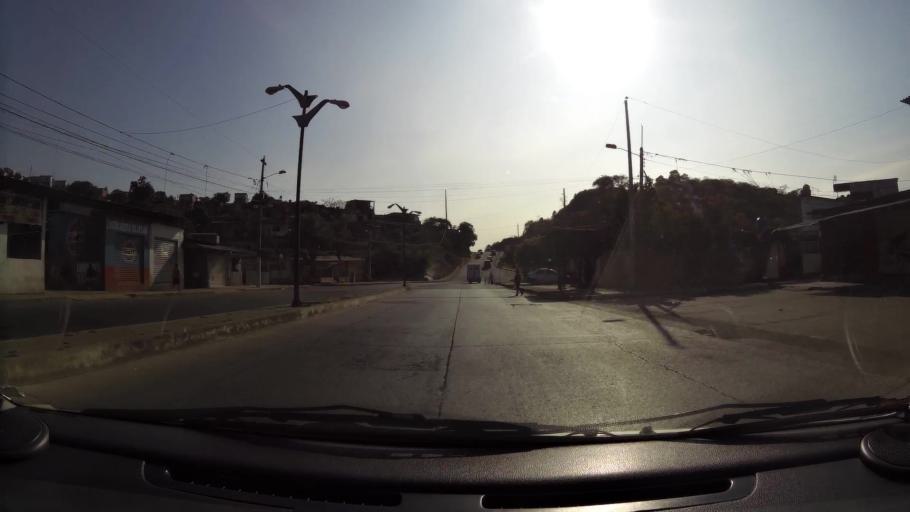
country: EC
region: Guayas
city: Eloy Alfaro
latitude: -2.1742
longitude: -79.8466
